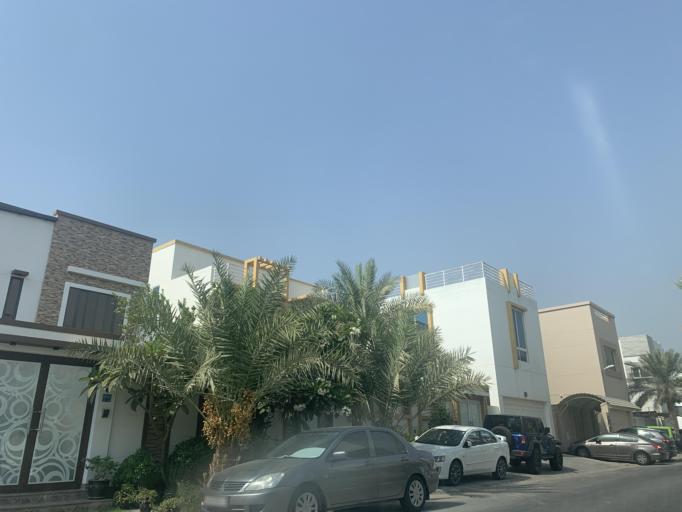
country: BH
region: Manama
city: Jidd Hafs
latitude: 26.2104
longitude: 50.4919
